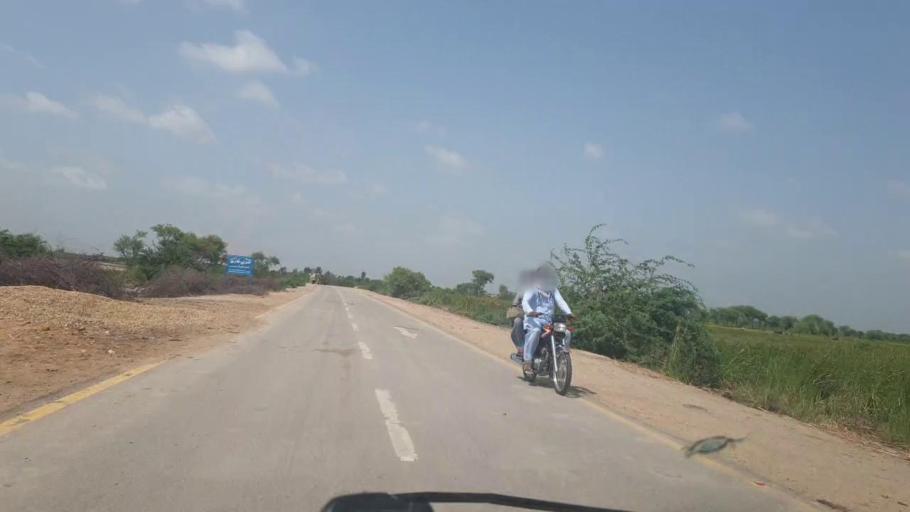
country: PK
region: Sindh
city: Berani
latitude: 25.6920
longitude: 68.9303
